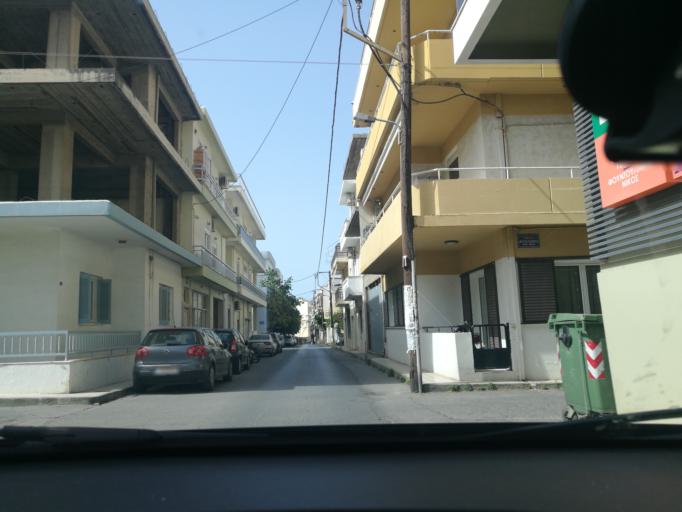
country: GR
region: Crete
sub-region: Nomos Irakleiou
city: Irakleion
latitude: 35.3272
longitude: 25.1306
